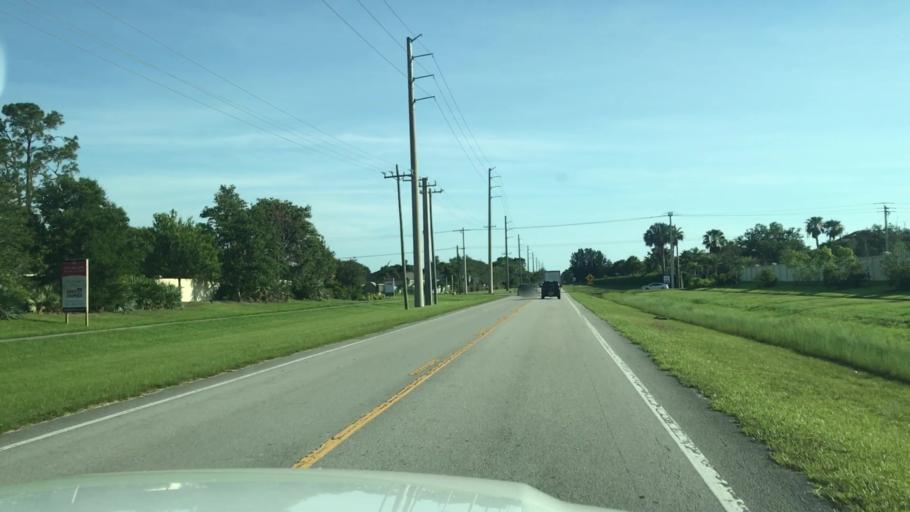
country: US
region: Florida
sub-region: Indian River County
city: Winter Beach
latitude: 27.7032
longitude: -80.4460
